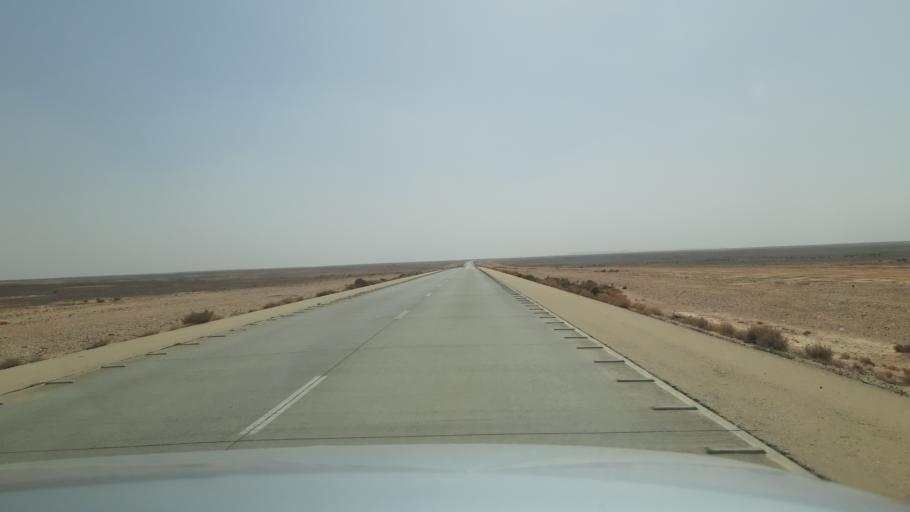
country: JO
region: Ma'an
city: Al Jafr
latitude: 30.9737
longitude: 36.6284
